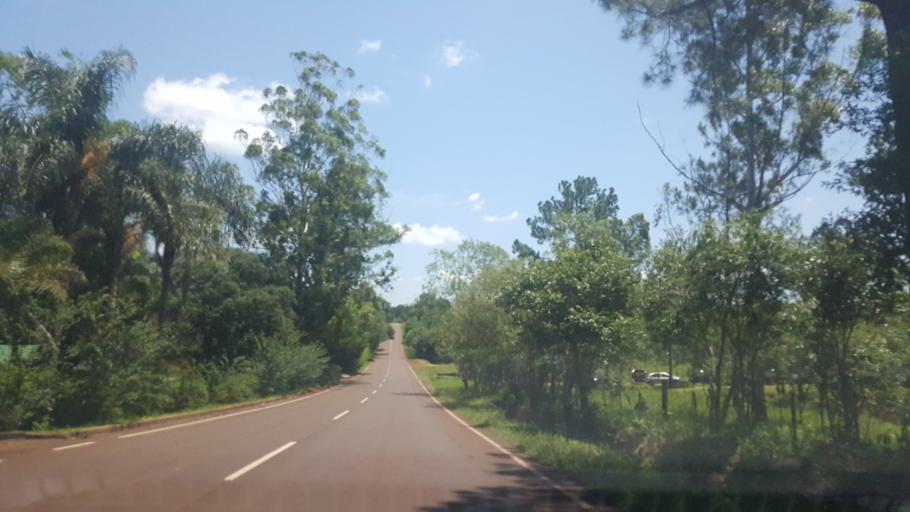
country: AR
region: Misiones
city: Garupa
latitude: -27.5039
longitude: -55.8527
